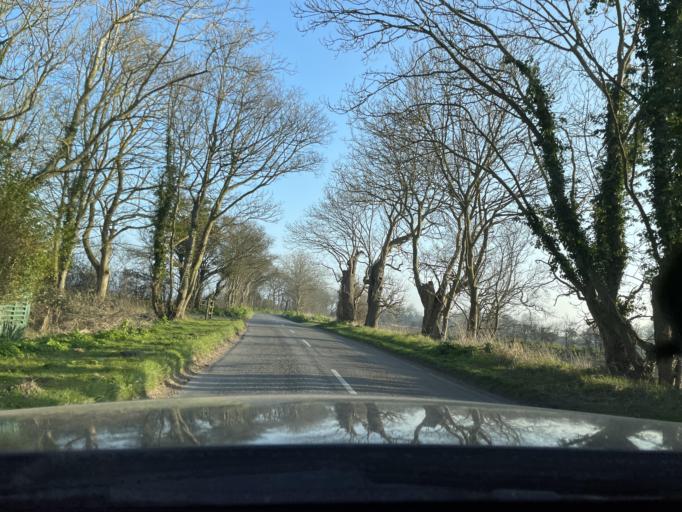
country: GB
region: England
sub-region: Norfolk
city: Martham
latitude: 52.7506
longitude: 1.6449
